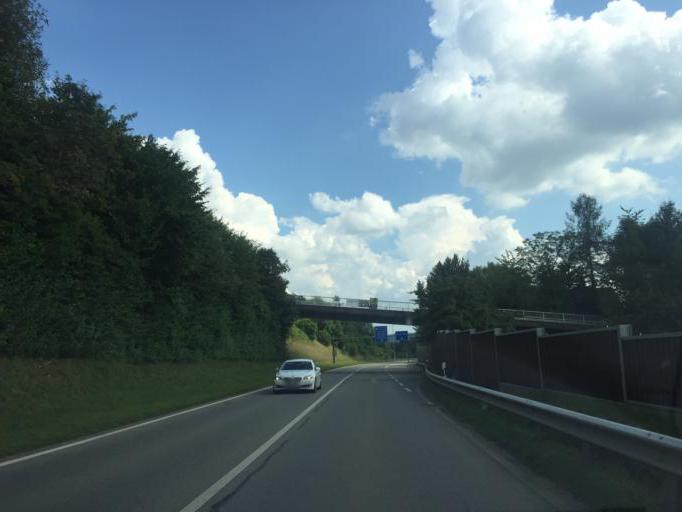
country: CH
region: Thurgau
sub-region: Frauenfeld District
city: Wagenhausen
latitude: 47.6769
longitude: 8.8344
